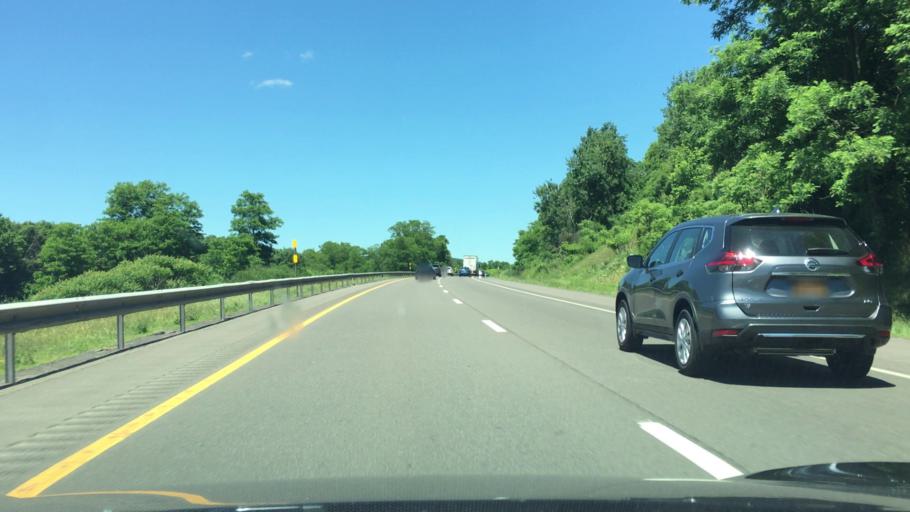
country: US
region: New York
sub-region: Cortland County
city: Homer
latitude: 42.6352
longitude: -76.1738
